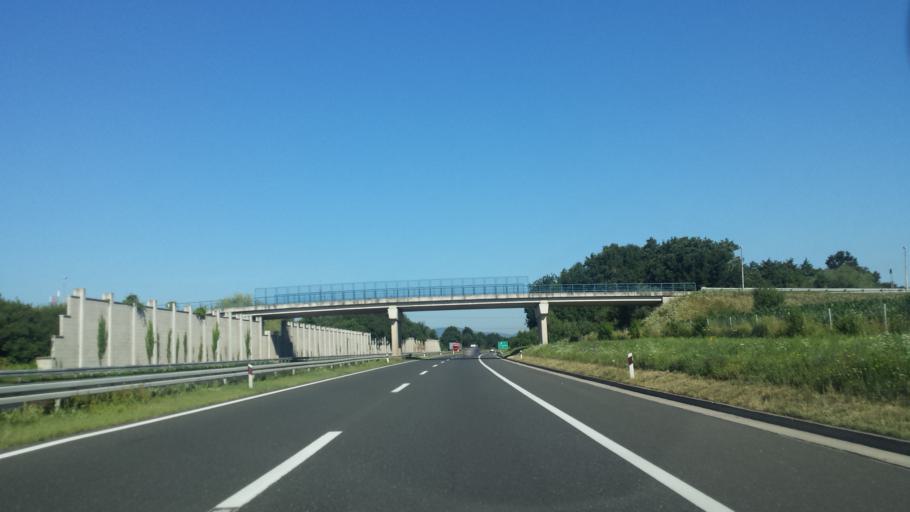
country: HR
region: Zagrebacka
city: Rakitje
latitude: 45.7875
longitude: 15.8027
